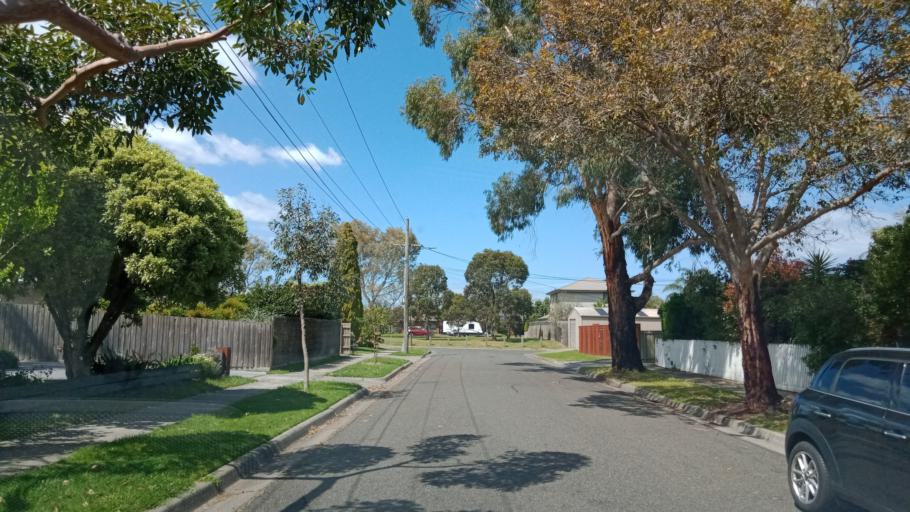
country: AU
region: Victoria
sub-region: Kingston
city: Chelsea Heights
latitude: -38.0494
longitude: 145.1403
